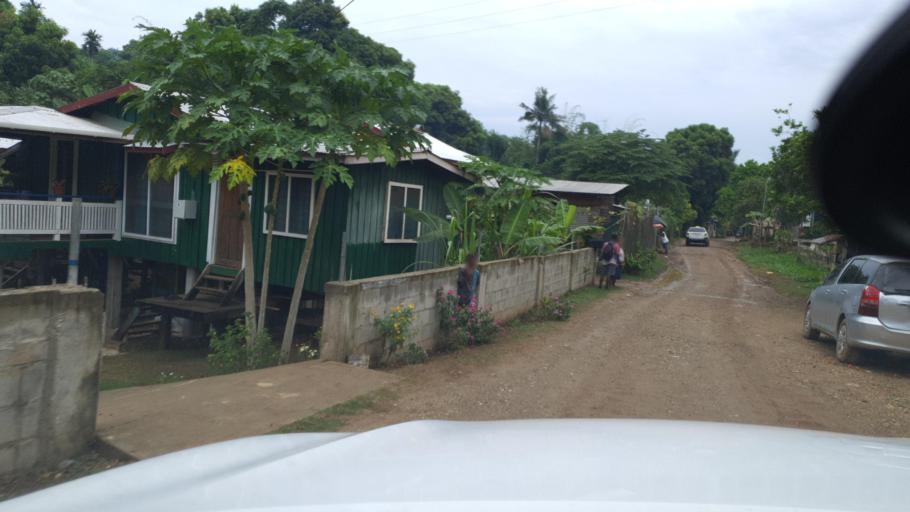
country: SB
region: Guadalcanal
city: Honiara
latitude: -9.4444
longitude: 159.9776
